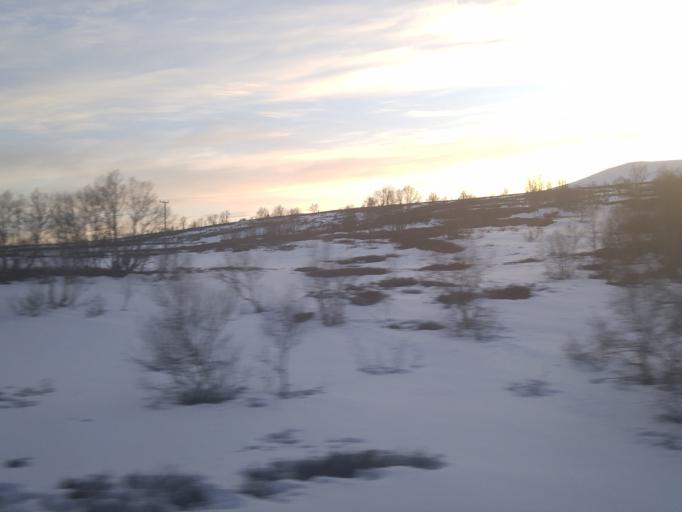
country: NO
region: Sor-Trondelag
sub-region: Oppdal
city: Oppdal
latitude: 62.2720
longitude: 9.5814
